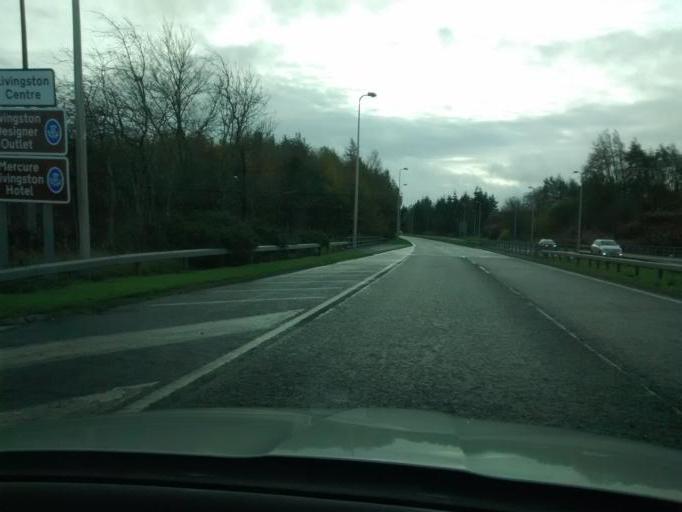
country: GB
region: Scotland
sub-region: West Lothian
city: Mid Calder
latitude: 55.8872
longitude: -3.5004
